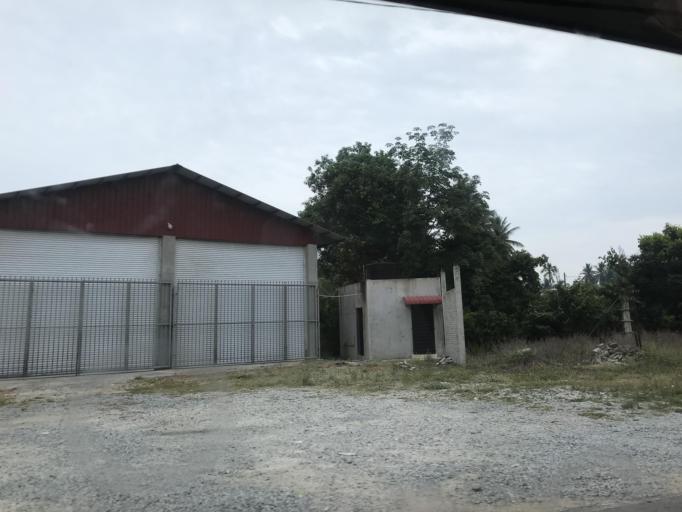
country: MY
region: Kelantan
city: Kota Bharu
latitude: 6.1760
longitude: 102.2239
